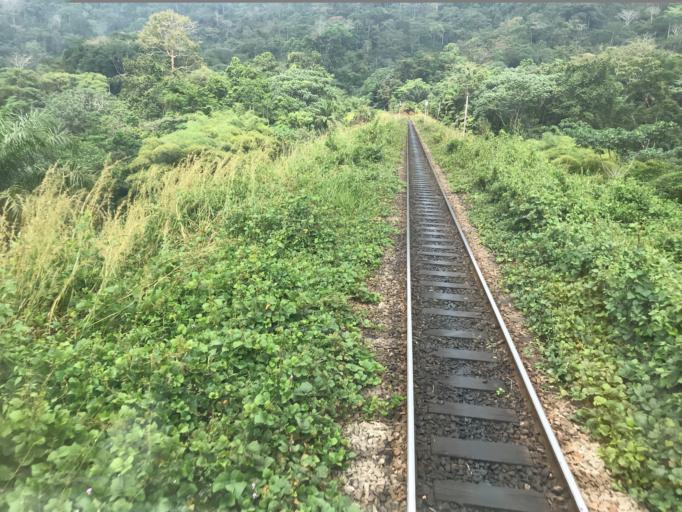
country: CM
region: Centre
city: Eseka
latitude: 3.5764
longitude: 10.8998
